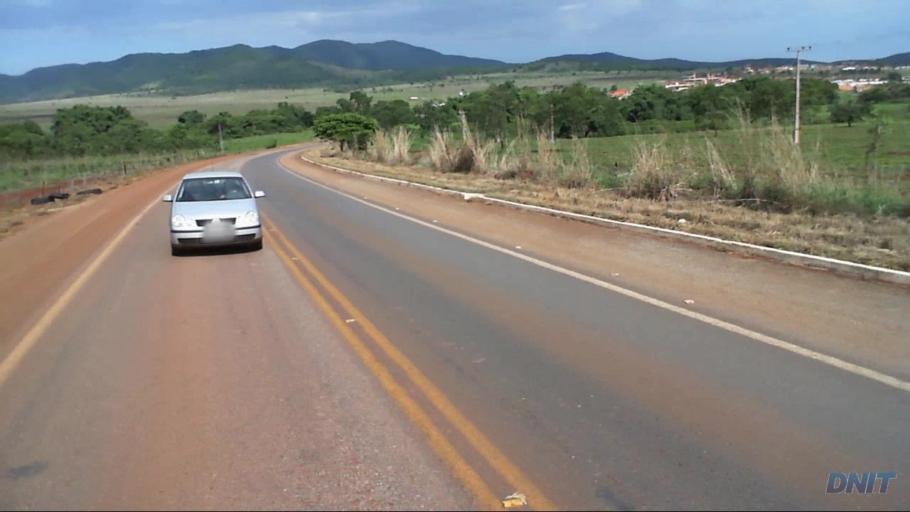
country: BR
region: Goias
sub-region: Barro Alto
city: Barro Alto
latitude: -14.9868
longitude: -48.9200
